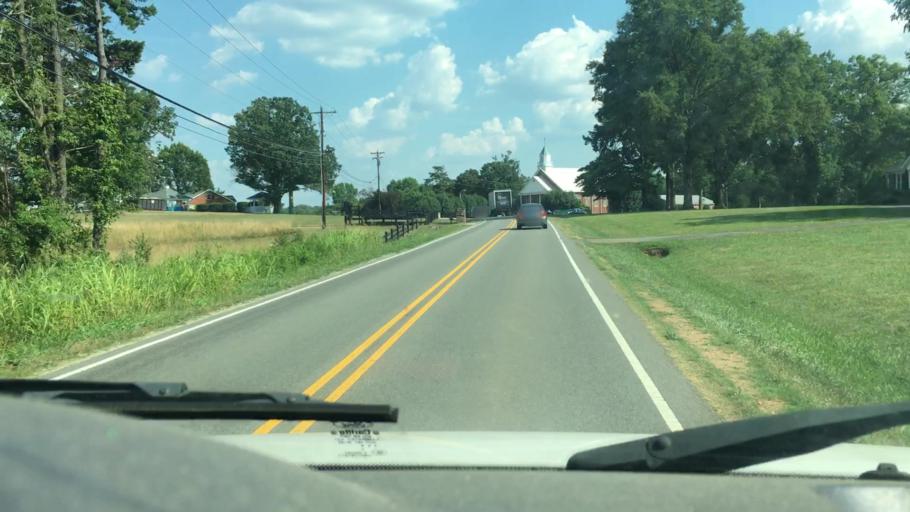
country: US
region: North Carolina
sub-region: Gaston County
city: Davidson
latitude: 35.4679
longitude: -80.8147
